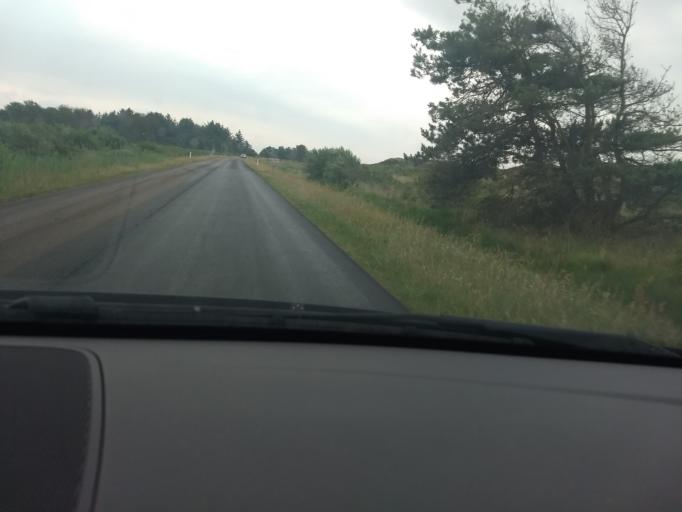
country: DK
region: South Denmark
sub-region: Fano Kommune
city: Nordby
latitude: 55.3719
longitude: 8.4535
